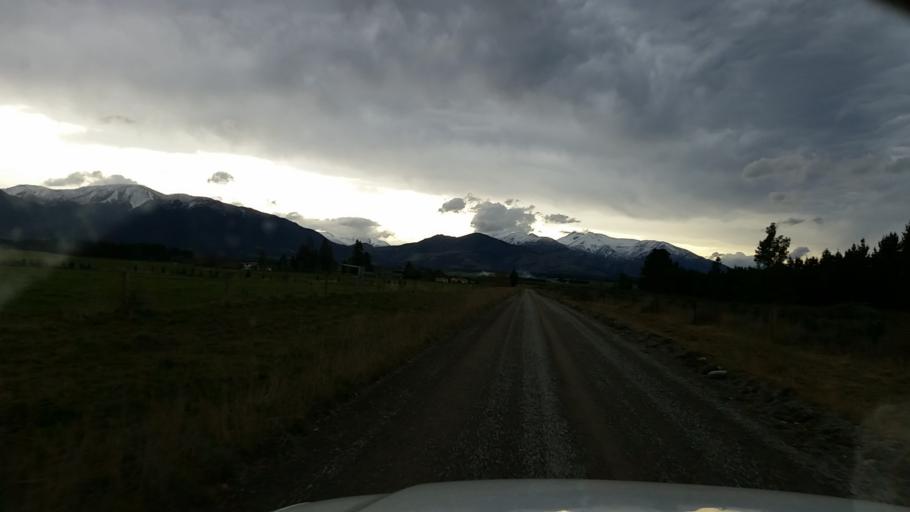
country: NZ
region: Canterbury
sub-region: Ashburton District
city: Methven
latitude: -43.7013
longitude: 171.4605
